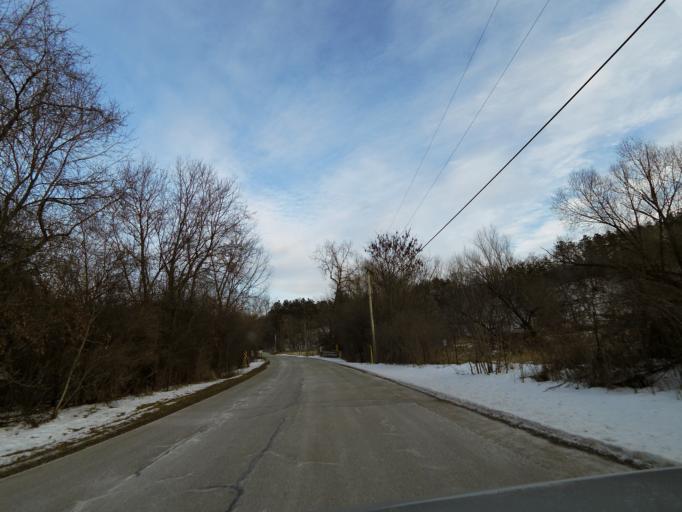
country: US
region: Minnesota
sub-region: Washington County
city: Afton
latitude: 44.9126
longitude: -92.8251
